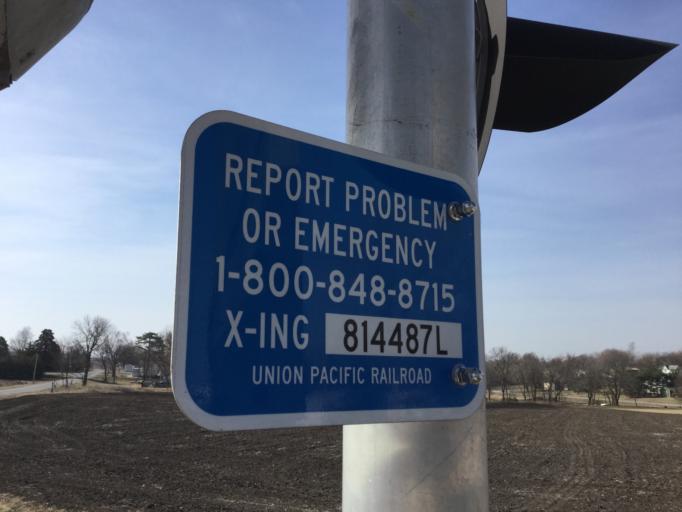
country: US
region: Kansas
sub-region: Nemaha County
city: Seneca
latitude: 39.8709
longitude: -96.2541
